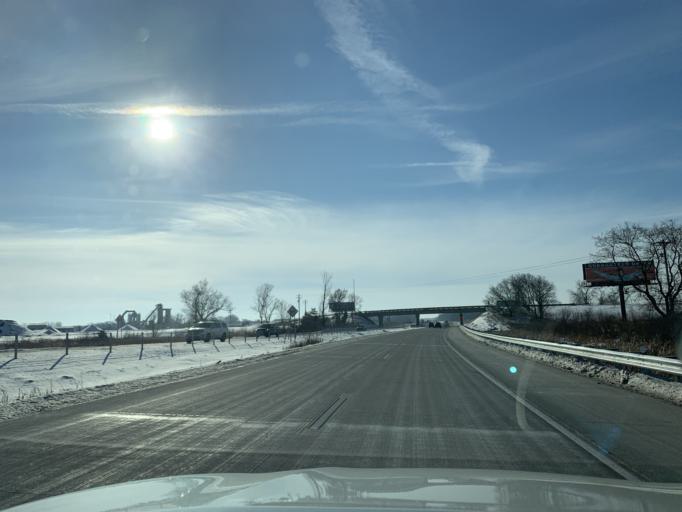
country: US
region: Minnesota
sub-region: Anoka County
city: Columbus
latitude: 45.2164
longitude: -93.0324
